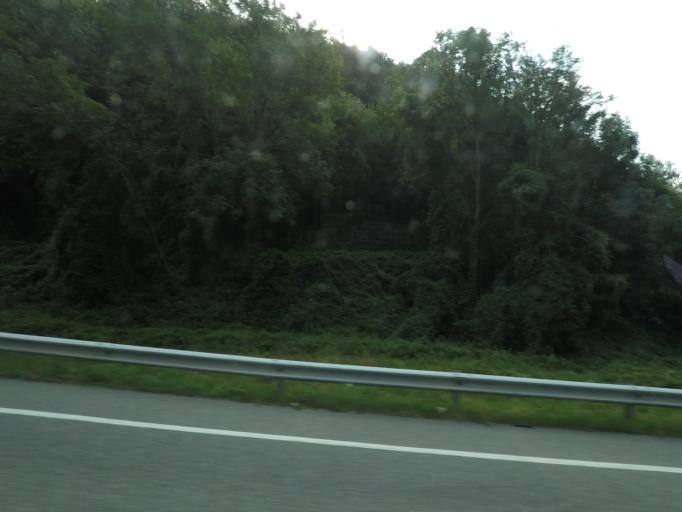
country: IT
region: Aosta Valley
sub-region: Valle d'Aosta
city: Antey-Saint-Andre
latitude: 45.7841
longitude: 7.5906
